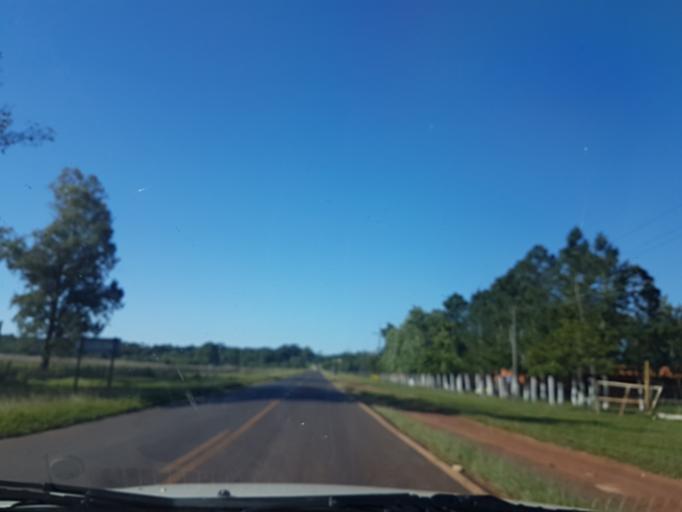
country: PY
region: Cordillera
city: Arroyos y Esteros
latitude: -25.0923
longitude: -57.0935
